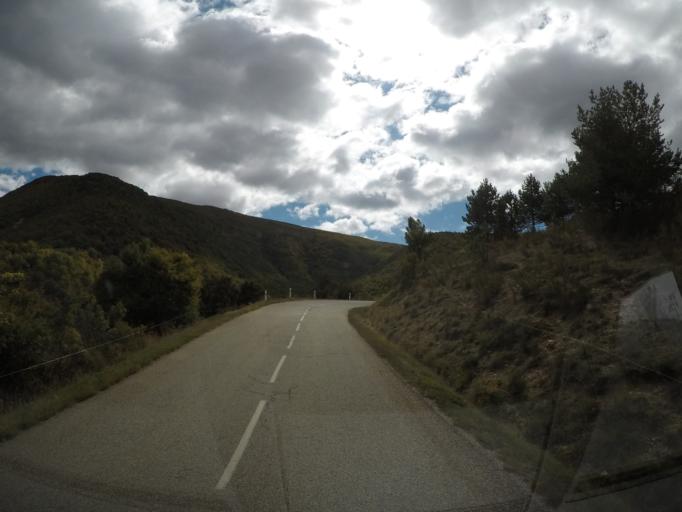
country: FR
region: Provence-Alpes-Cote d'Azur
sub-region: Departement du Vaucluse
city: Sault
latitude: 44.1848
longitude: 5.5315
